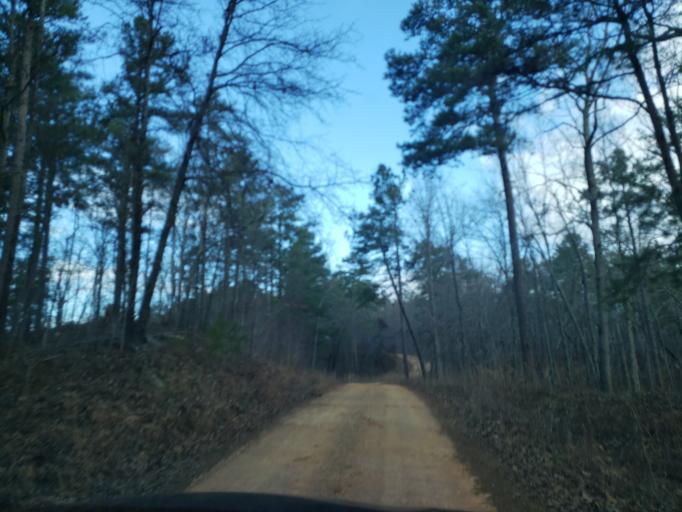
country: US
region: Alabama
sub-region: Cleburne County
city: Heflin
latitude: 33.6883
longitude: -85.6359
